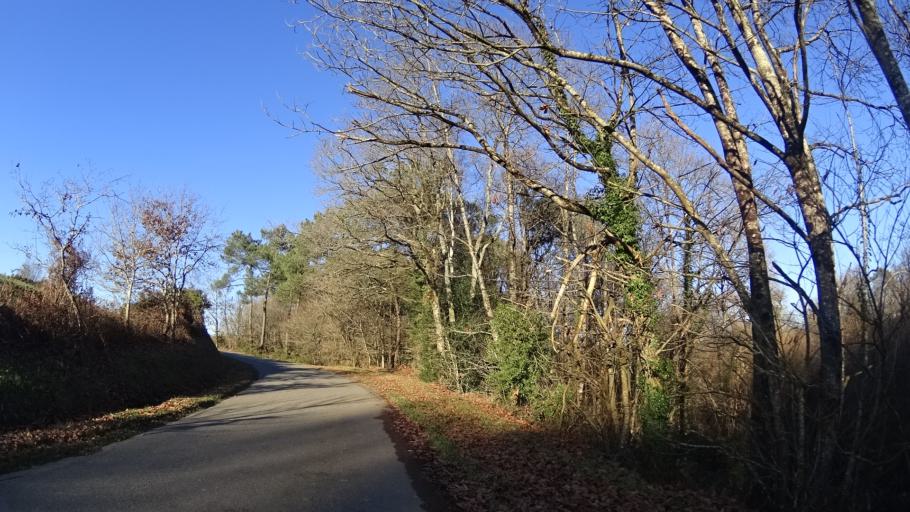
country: FR
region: Brittany
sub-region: Departement du Morbihan
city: Saint-Jacut-les-Pins
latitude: 47.6603
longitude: -2.2062
